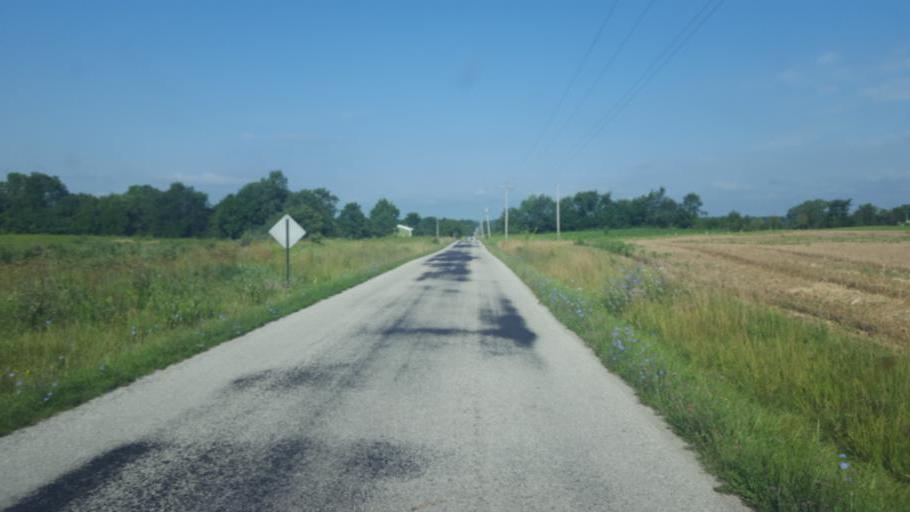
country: US
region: Ohio
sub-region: Morrow County
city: Mount Gilead
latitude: 40.6244
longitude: -82.7495
